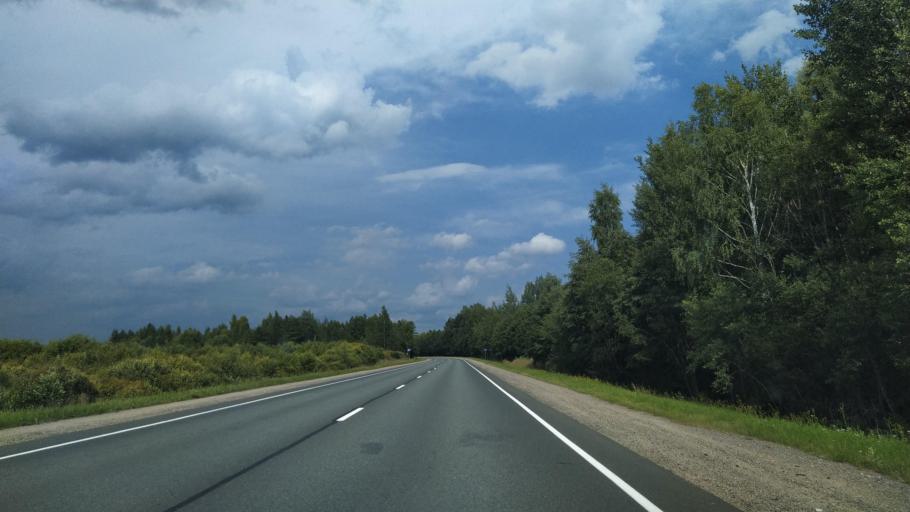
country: RU
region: Pskov
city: Porkhov
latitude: 57.9456
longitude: 29.6545
